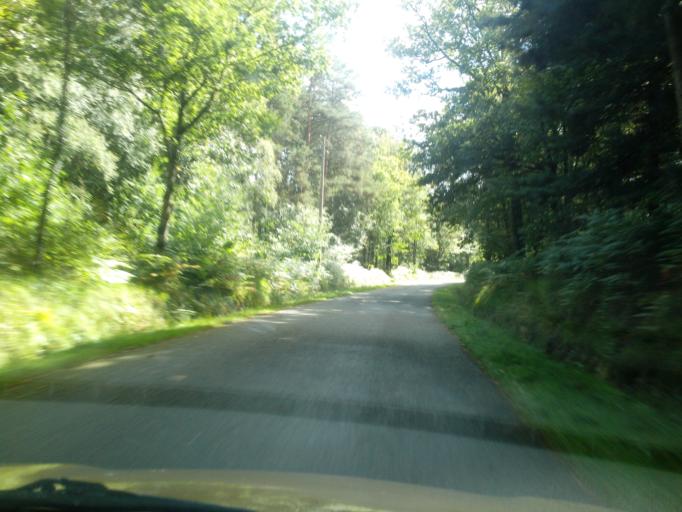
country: FR
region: Brittany
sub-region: Departement des Cotes-d'Armor
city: Merdrignac
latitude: 48.1272
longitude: -2.3880
